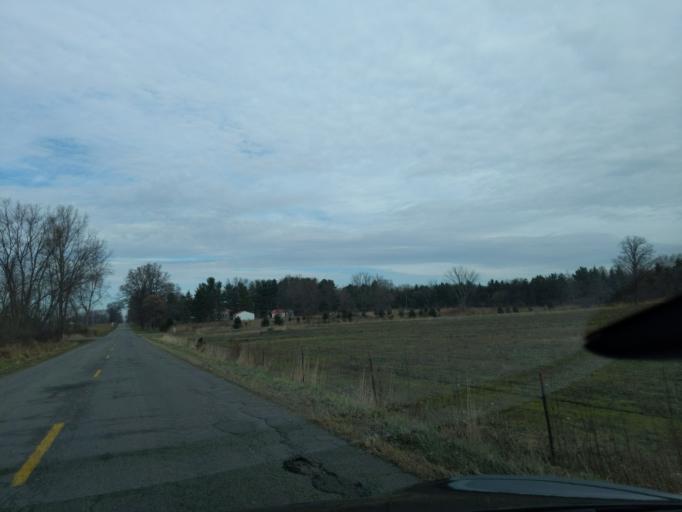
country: US
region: Michigan
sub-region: Ingham County
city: Leslie
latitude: 42.4644
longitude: -84.5020
